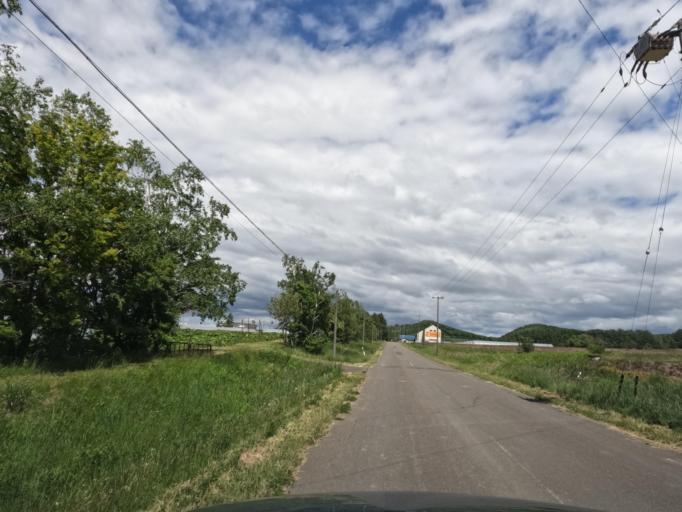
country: JP
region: Hokkaido
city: Iwamizawa
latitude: 43.1362
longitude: 141.8065
